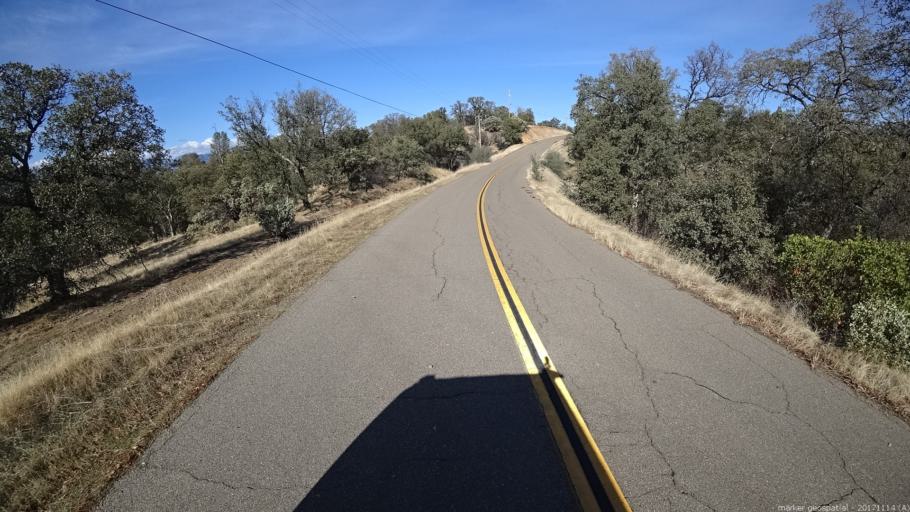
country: US
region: California
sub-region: Shasta County
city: Anderson
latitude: 40.4057
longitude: -122.4106
